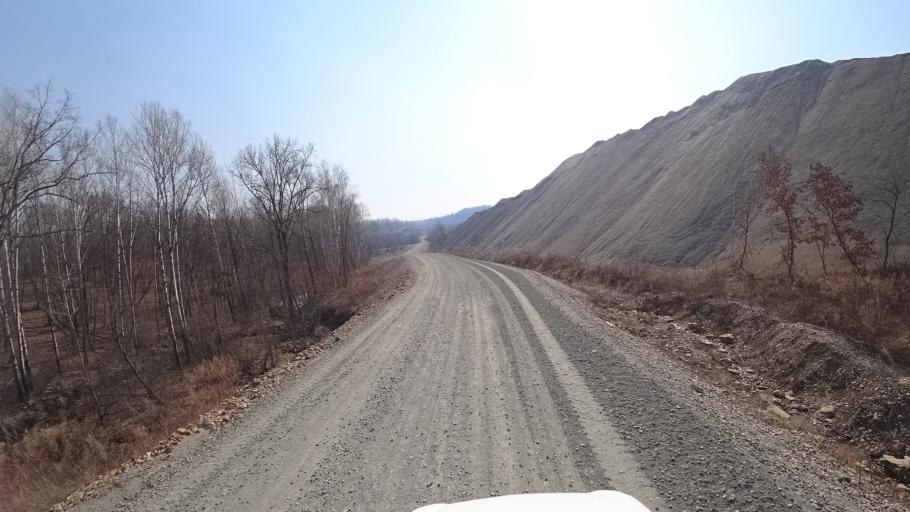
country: RU
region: Amur
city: Novobureyskiy
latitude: 49.7996
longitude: 129.9588
